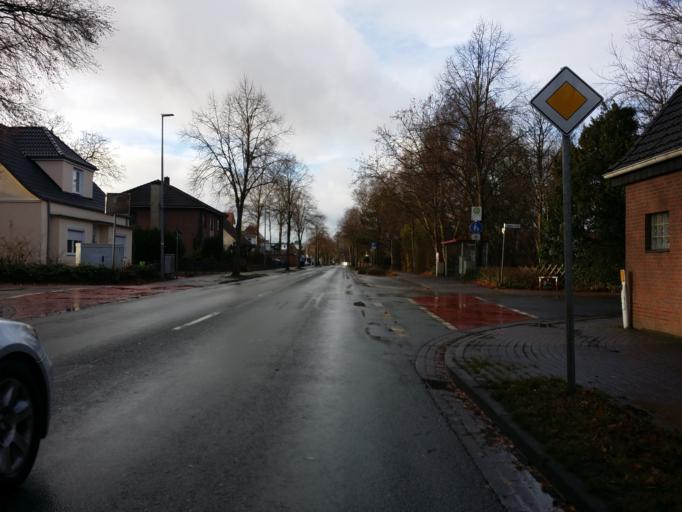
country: DE
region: Lower Saxony
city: Syke
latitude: 52.9876
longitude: 8.8241
